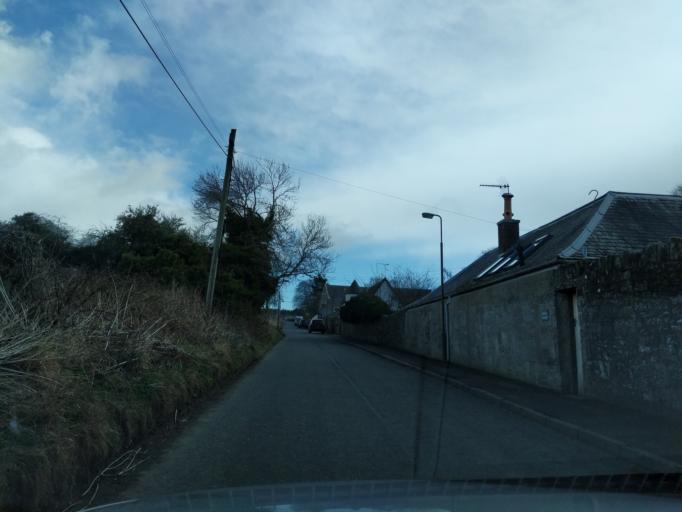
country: GB
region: Scotland
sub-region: Edinburgh
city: Balerno
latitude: 55.8772
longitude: -3.3272
